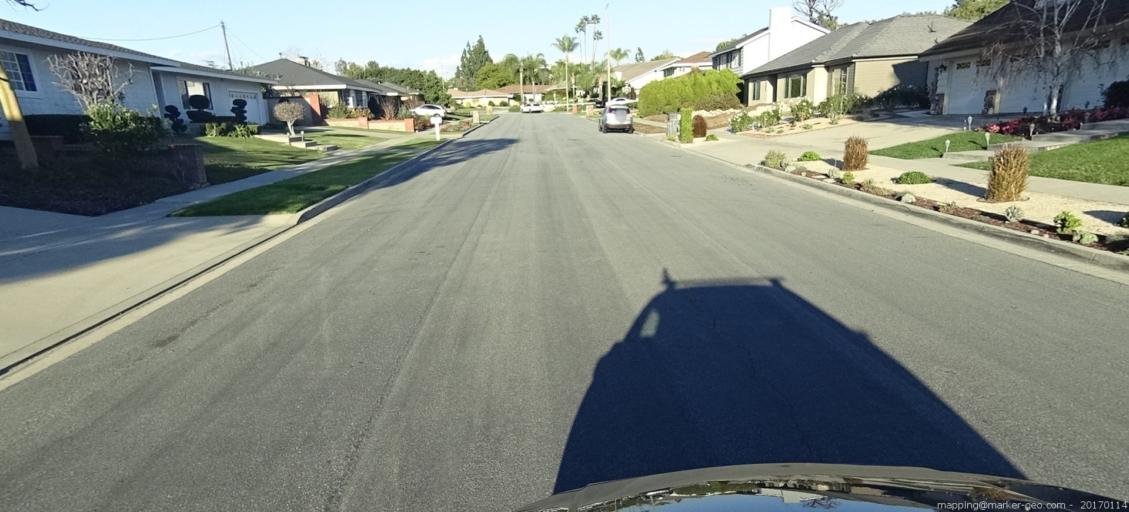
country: US
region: California
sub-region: Orange County
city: Tustin
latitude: 33.7648
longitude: -117.8177
